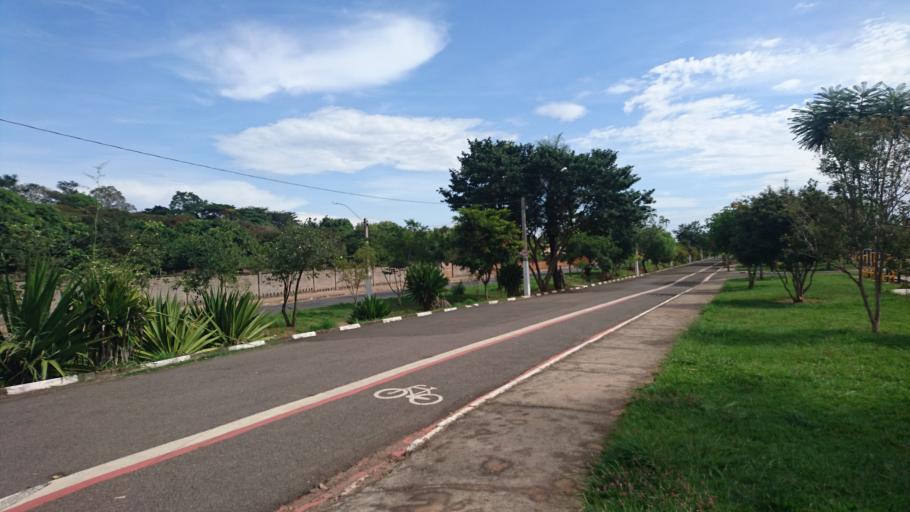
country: BR
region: Sao Paulo
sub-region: Casa Branca
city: Casa Branca
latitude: -21.7810
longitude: -47.0883
